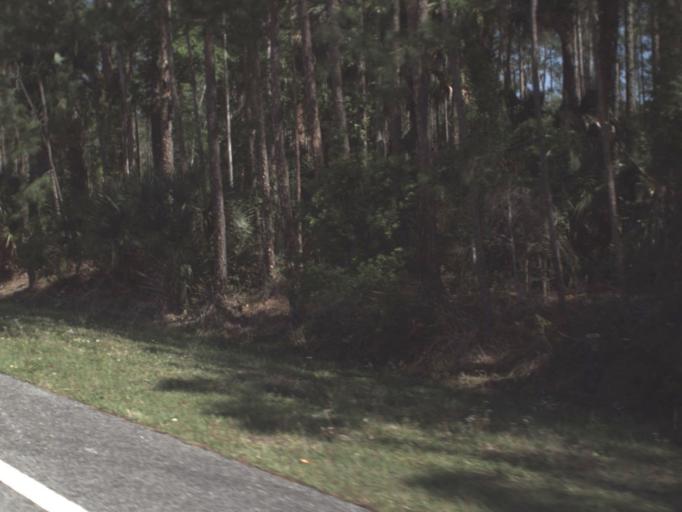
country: US
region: Florida
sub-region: Volusia County
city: Ormond-by-the-Sea
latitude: 29.3632
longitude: -81.1680
